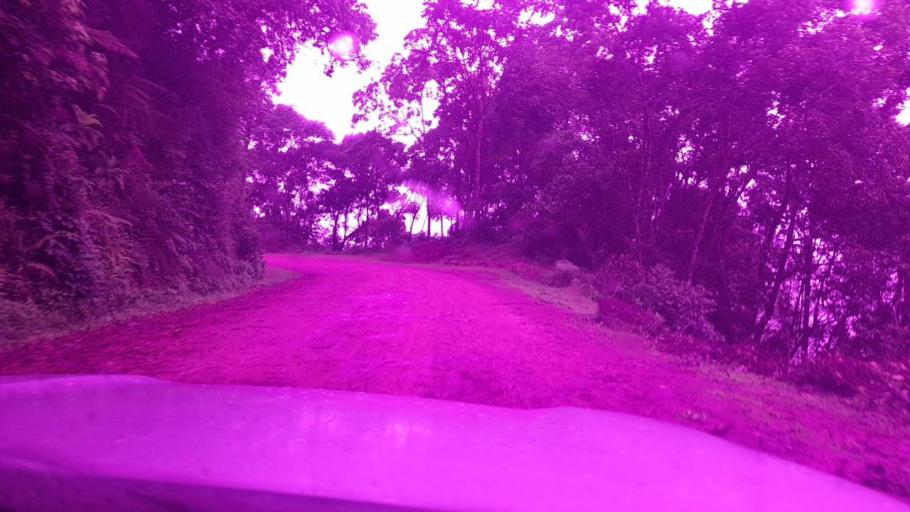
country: ET
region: Southern Nations, Nationalities, and People's Region
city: Bonga
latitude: 7.5097
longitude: 36.0627
